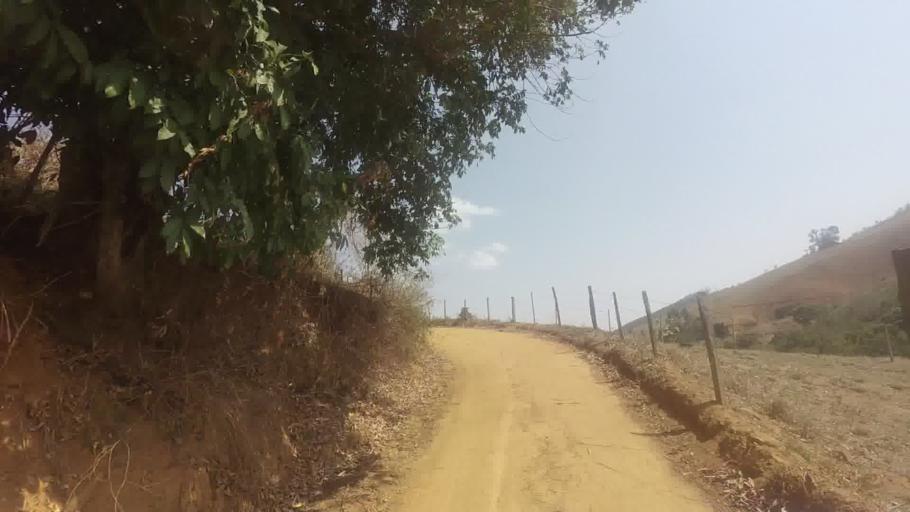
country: BR
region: Espirito Santo
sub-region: Sao Jose Do Calcado
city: Sao Jose do Calcado
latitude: -21.0142
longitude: -41.5143
